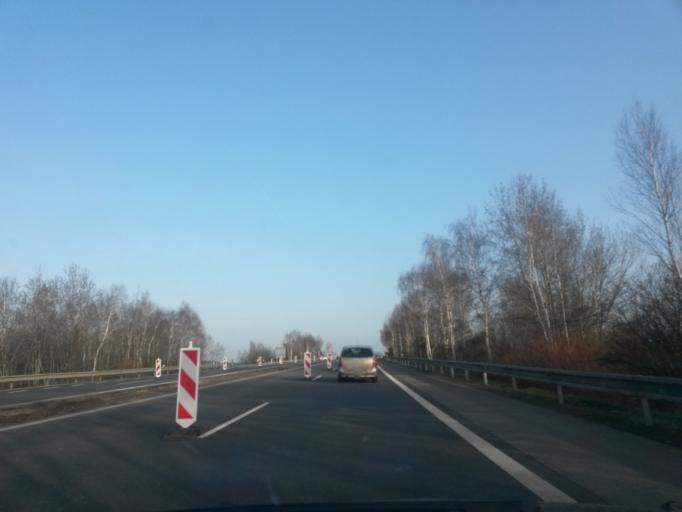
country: CZ
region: Central Bohemia
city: Kacice
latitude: 50.1546
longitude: 13.9771
